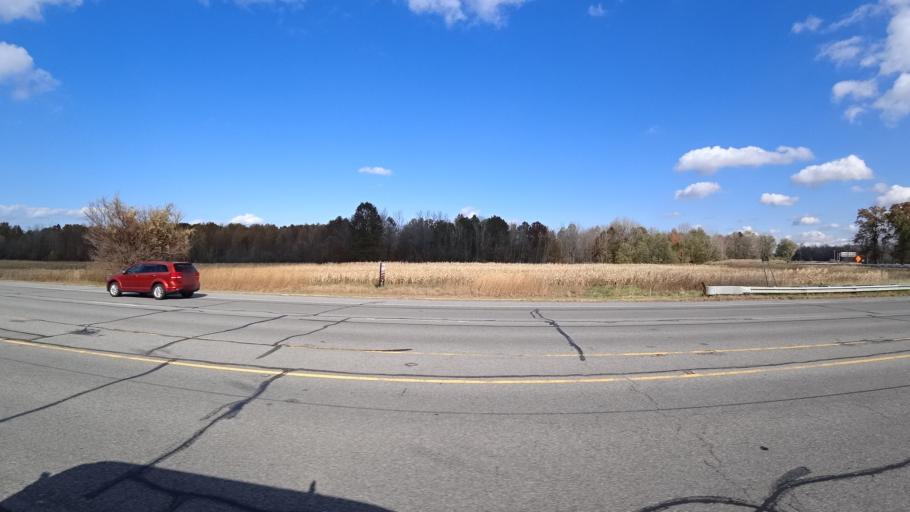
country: US
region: Indiana
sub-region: LaPorte County
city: Trail Creek
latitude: 41.6990
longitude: -86.8310
